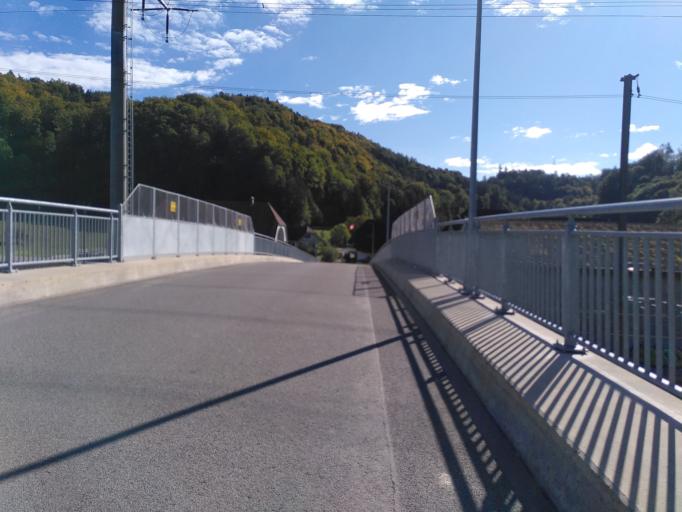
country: CH
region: Bern
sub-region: Oberaargau
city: Seeberg
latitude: 47.1429
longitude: 7.6955
